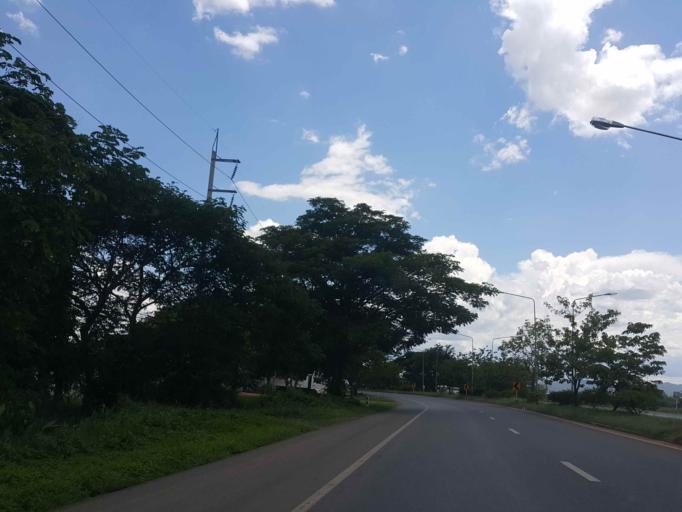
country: TH
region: Phrae
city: Nong Muang Khai
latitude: 18.2239
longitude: 100.2007
